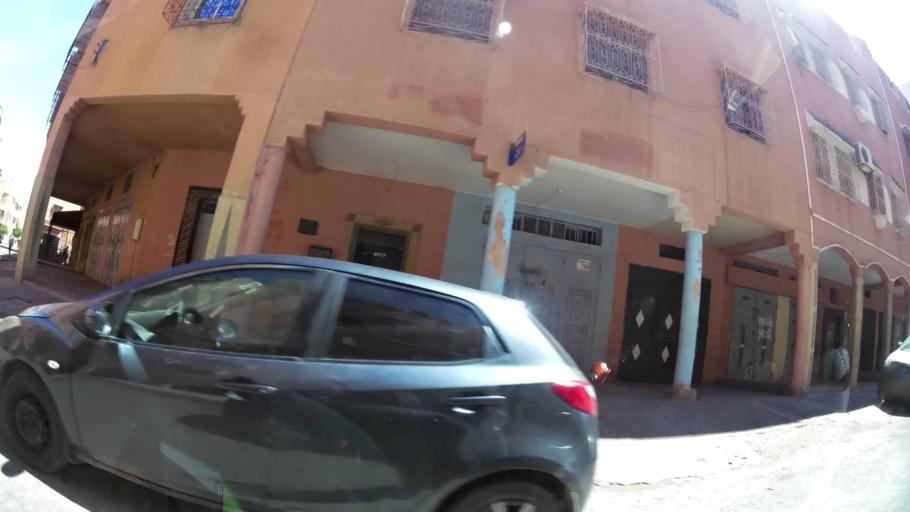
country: MA
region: Marrakech-Tensift-Al Haouz
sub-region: Marrakech
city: Marrakesh
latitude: 31.6295
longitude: -8.0681
